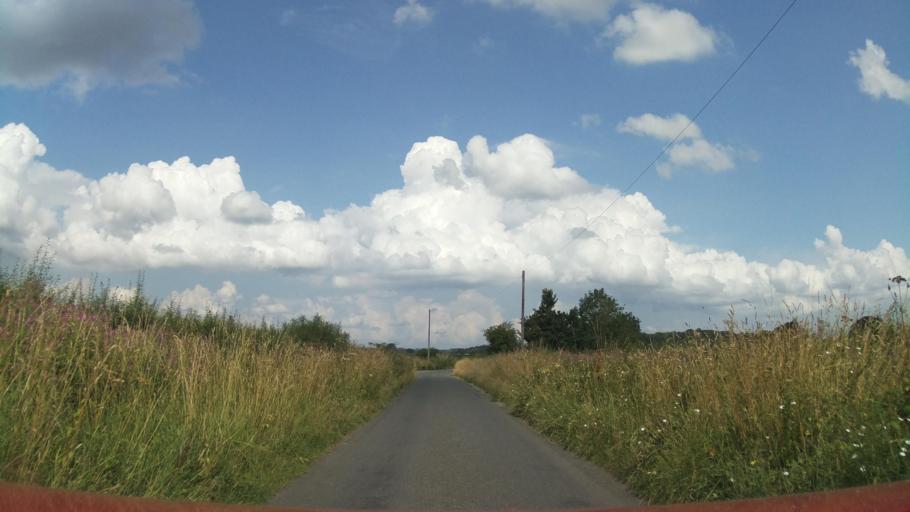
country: GB
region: England
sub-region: Wiltshire
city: Malmesbury
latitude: 51.5621
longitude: -2.1208
